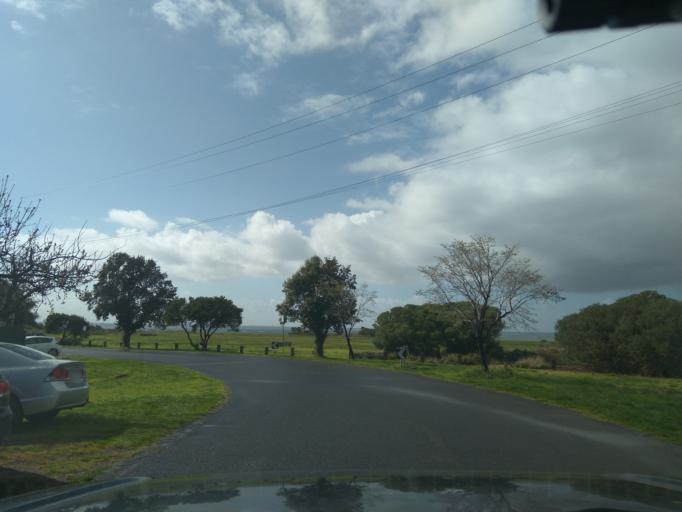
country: AU
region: Victoria
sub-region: Hobsons Bay
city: Williamstown
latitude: -37.8675
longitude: 144.9077
